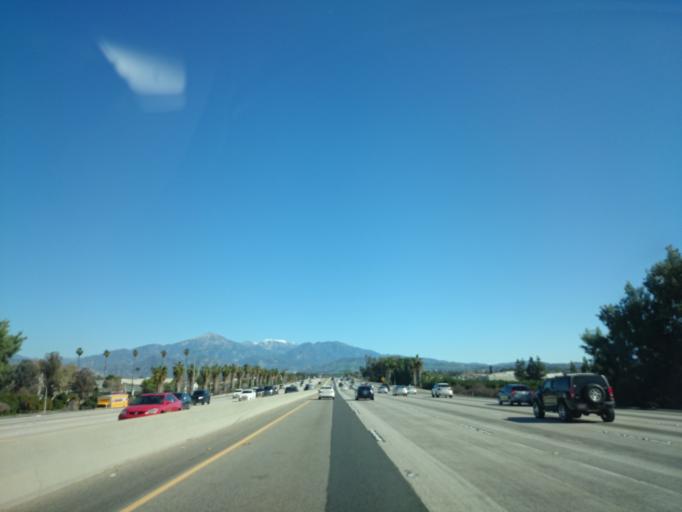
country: US
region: California
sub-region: San Bernardino County
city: Loma Linda
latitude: 34.0666
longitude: -117.2251
